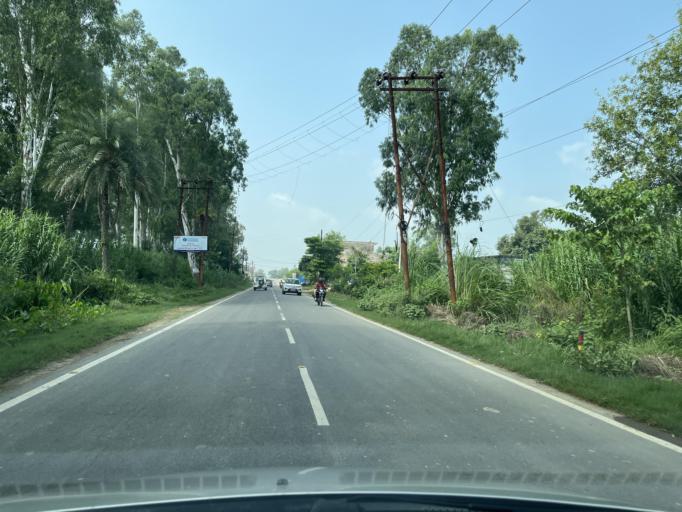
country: IN
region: Uttarakhand
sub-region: Udham Singh Nagar
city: Bazpur
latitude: 29.1669
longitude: 79.1612
